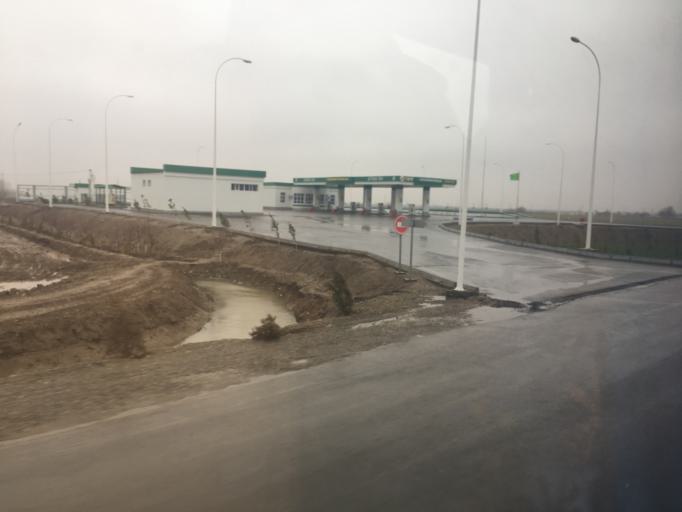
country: TM
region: Lebap
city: Turkmenabat
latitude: 39.0096
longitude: 63.5953
